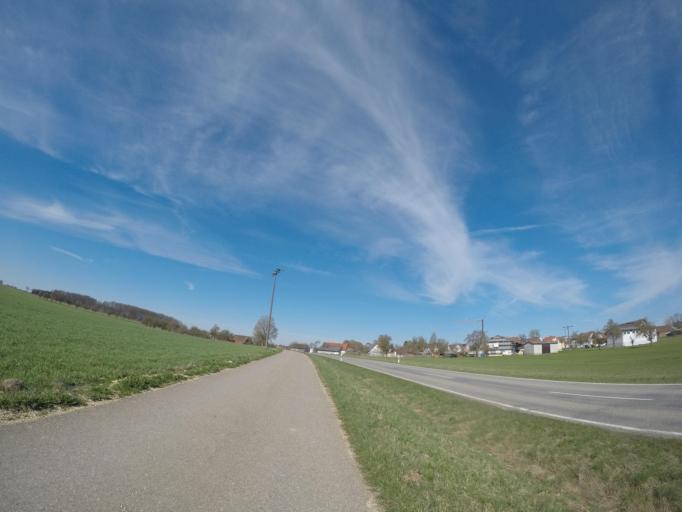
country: DE
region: Baden-Wuerttemberg
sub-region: Tuebingen Region
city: Mehrstetten
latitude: 48.3481
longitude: 9.6121
